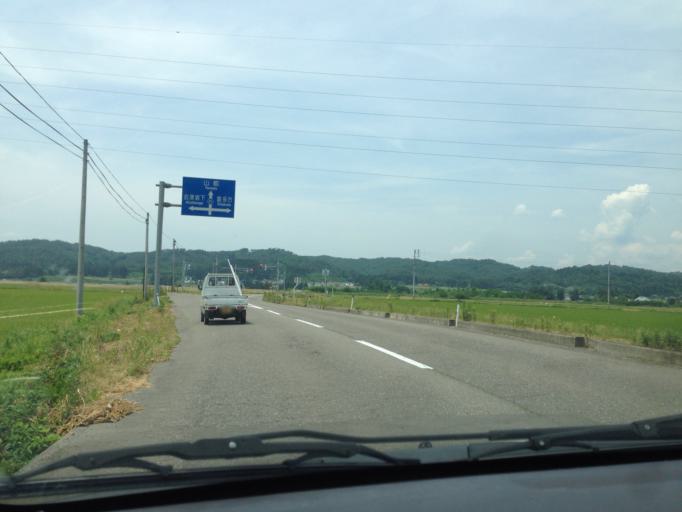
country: JP
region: Fukushima
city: Kitakata
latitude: 37.6158
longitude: 139.8492
